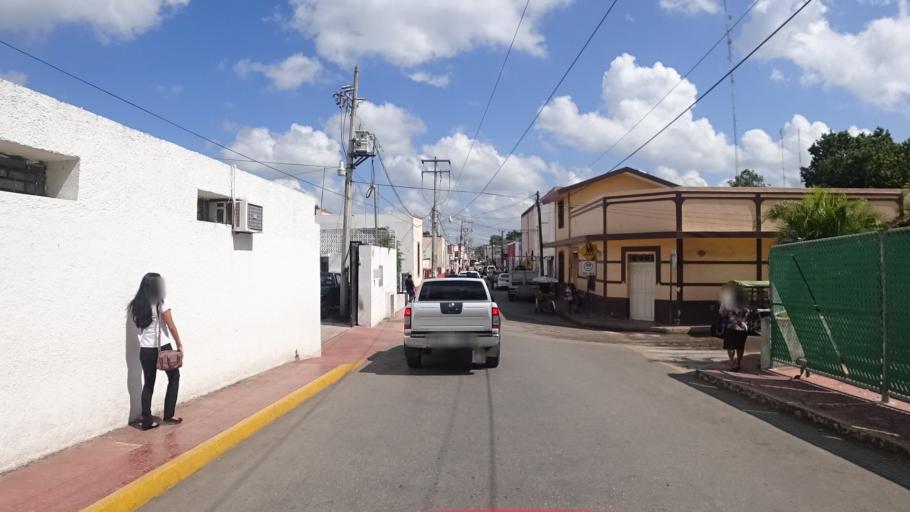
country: MX
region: Yucatan
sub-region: Tizimin
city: Tizimin
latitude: 21.1433
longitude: -88.1517
